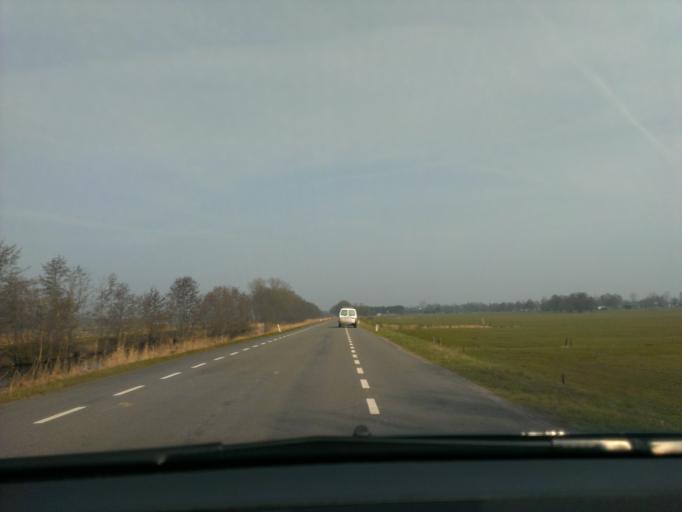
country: NL
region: Gelderland
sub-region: Gemeente Epe
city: Emst
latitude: 52.3179
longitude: 6.0109
